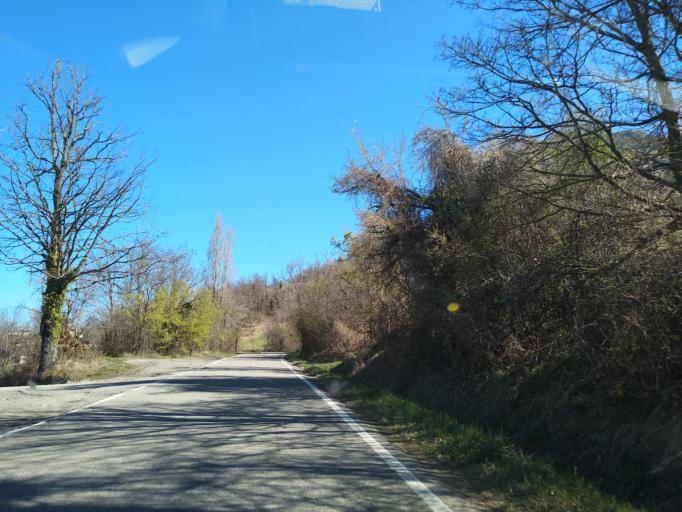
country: IT
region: Emilia-Romagna
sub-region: Provincia di Reggio Emilia
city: Castelnovo ne'Monti
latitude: 44.4167
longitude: 10.4026
